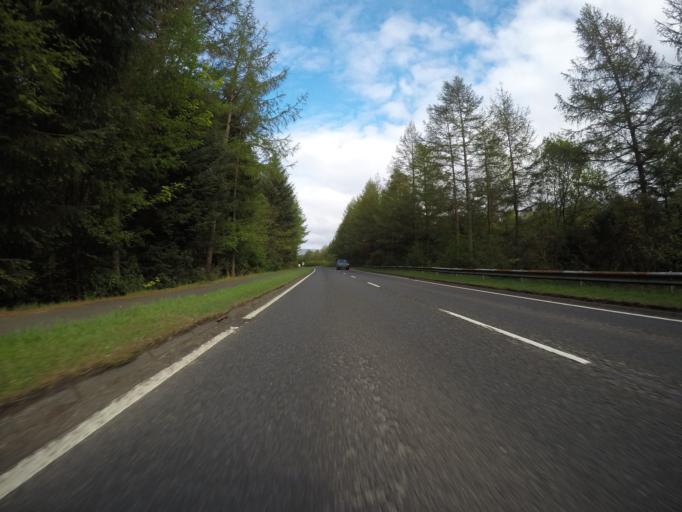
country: GB
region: Scotland
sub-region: Highland
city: Fort William
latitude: 56.6800
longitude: -5.1593
